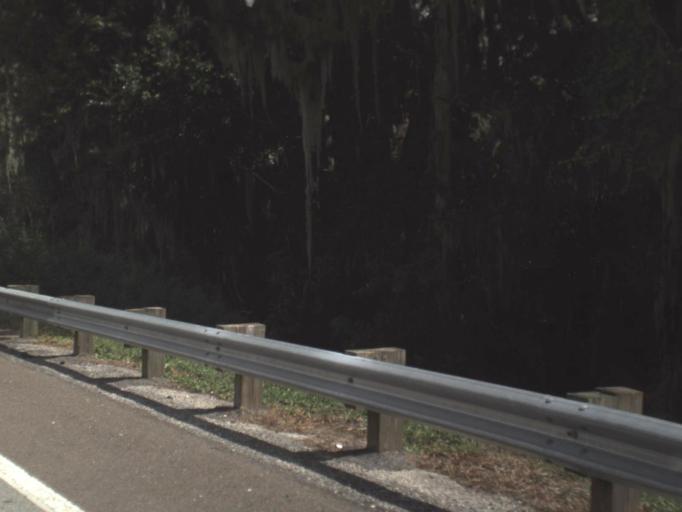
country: US
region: Florida
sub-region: Hardee County
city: Zolfo Springs
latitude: 27.5000
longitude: -81.8079
